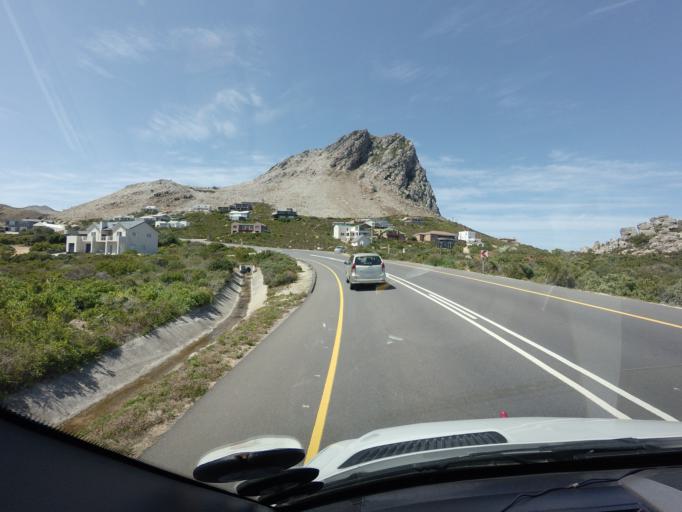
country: ZA
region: Western Cape
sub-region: Overberg District Municipality
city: Grabouw
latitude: -34.3012
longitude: 18.8202
